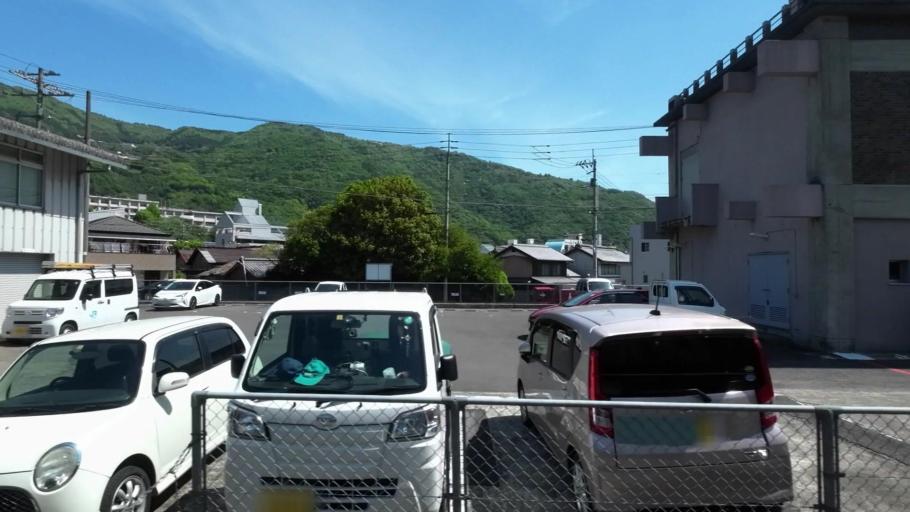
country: JP
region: Tokushima
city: Ikedacho
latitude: 34.0275
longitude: 133.8041
